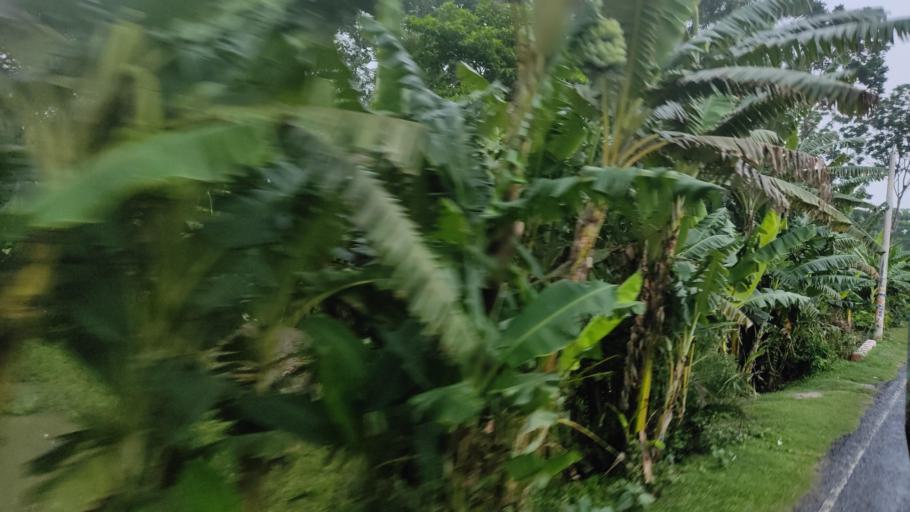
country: BD
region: Barisal
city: Bhandaria
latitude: 22.3075
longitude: 90.3247
